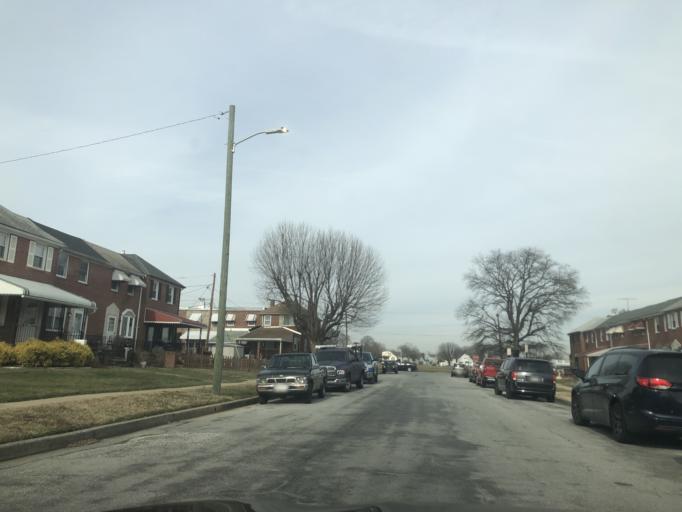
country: US
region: Maryland
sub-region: Baltimore County
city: Dundalk
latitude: 39.2741
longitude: -76.4975
